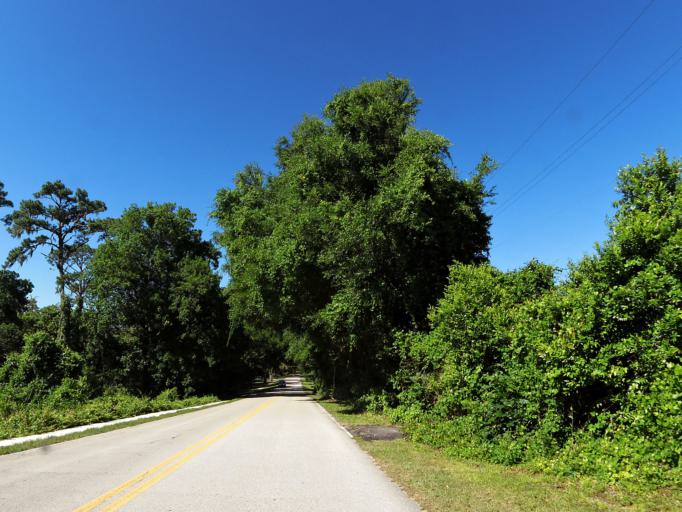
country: US
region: Florida
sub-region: Duval County
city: Atlantic Beach
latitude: 30.3819
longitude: -81.4974
